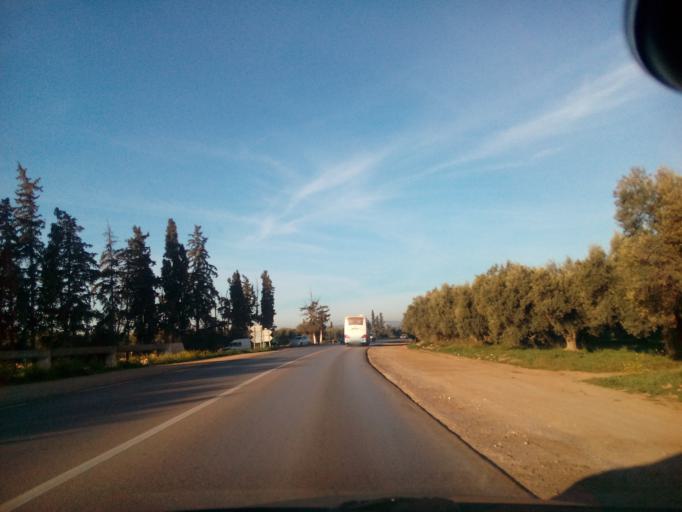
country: DZ
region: Relizane
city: Relizane
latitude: 35.7123
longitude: 0.3442
